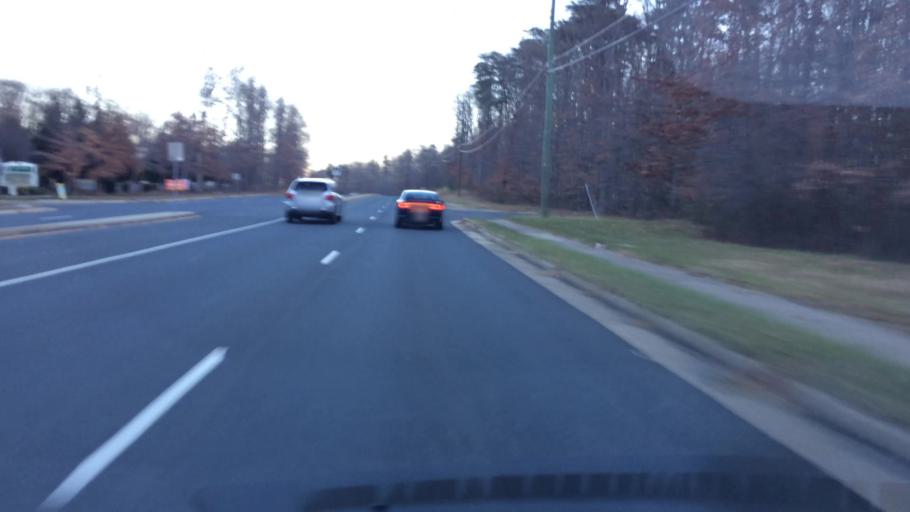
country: US
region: Virginia
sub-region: City of Fairfax
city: Fairfax
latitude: 38.8391
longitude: -77.3431
